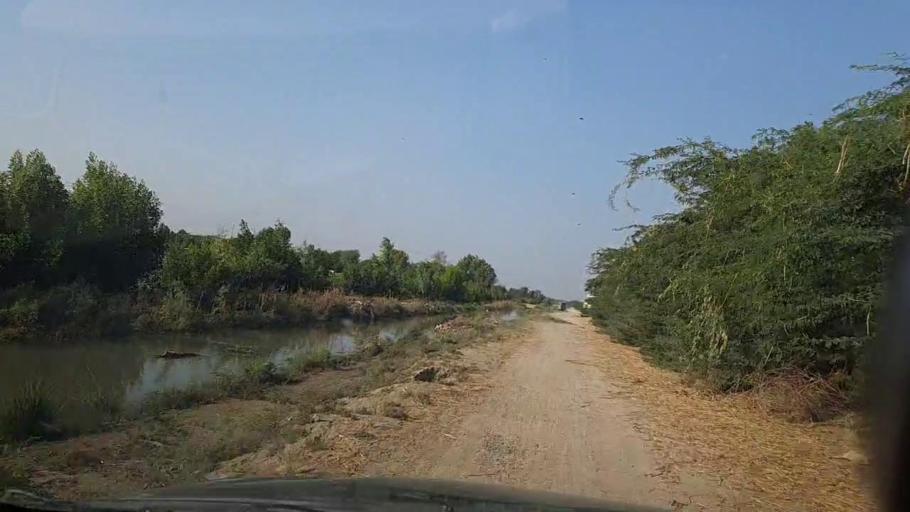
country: PK
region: Sindh
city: Thatta
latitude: 24.6114
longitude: 67.8763
